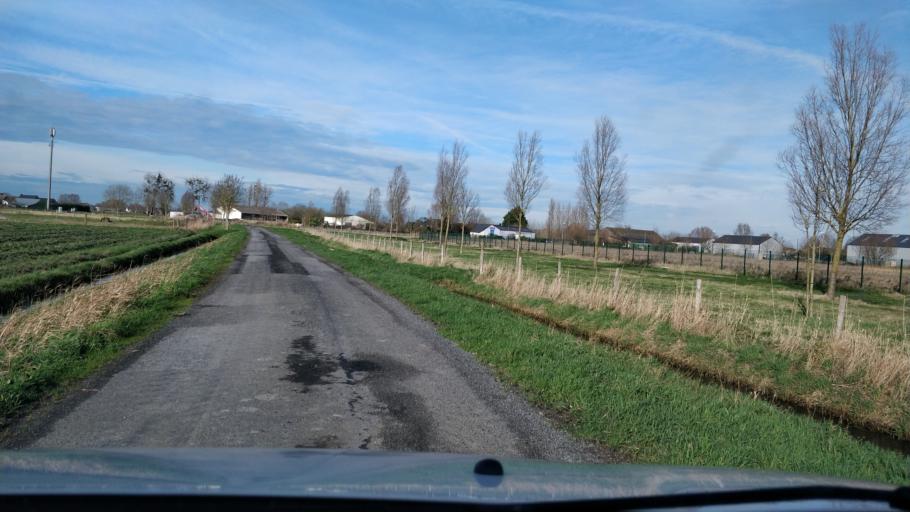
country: FR
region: Brittany
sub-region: Departement d'Ille-et-Vilaine
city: La Fresnais
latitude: 48.5807
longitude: -1.8309
